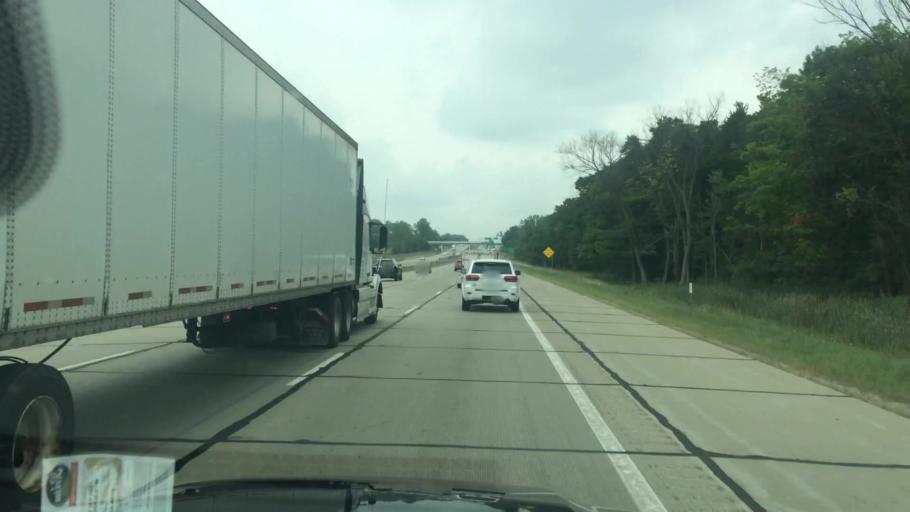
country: US
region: Michigan
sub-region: Eaton County
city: Waverly
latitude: 42.7625
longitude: -84.6681
